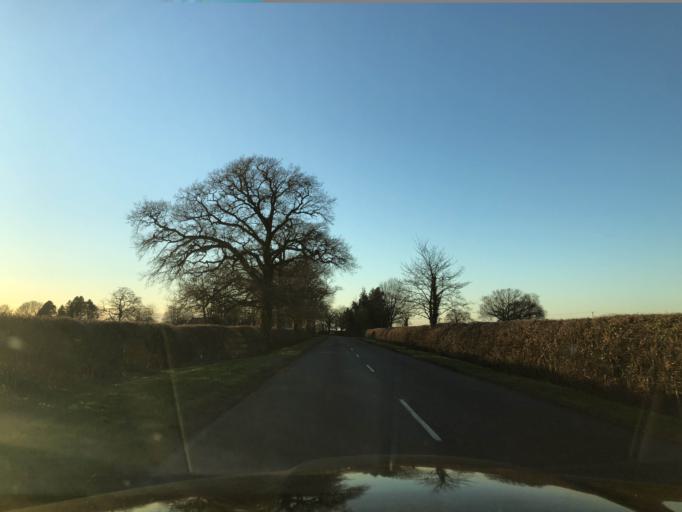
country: GB
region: England
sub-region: Warwickshire
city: Harbury
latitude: 52.2262
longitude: -1.4575
